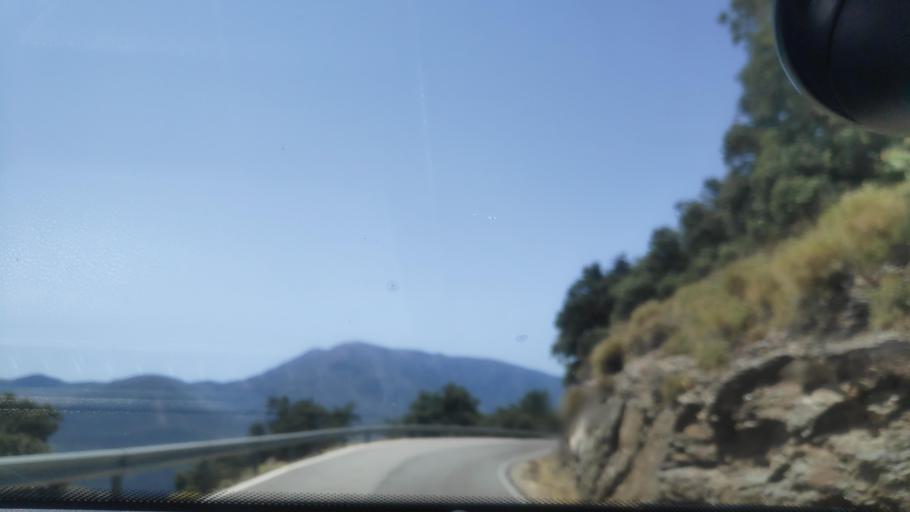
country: ES
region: Andalusia
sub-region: Provincia de Granada
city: Pampaneira
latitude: 36.9270
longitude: -3.3480
